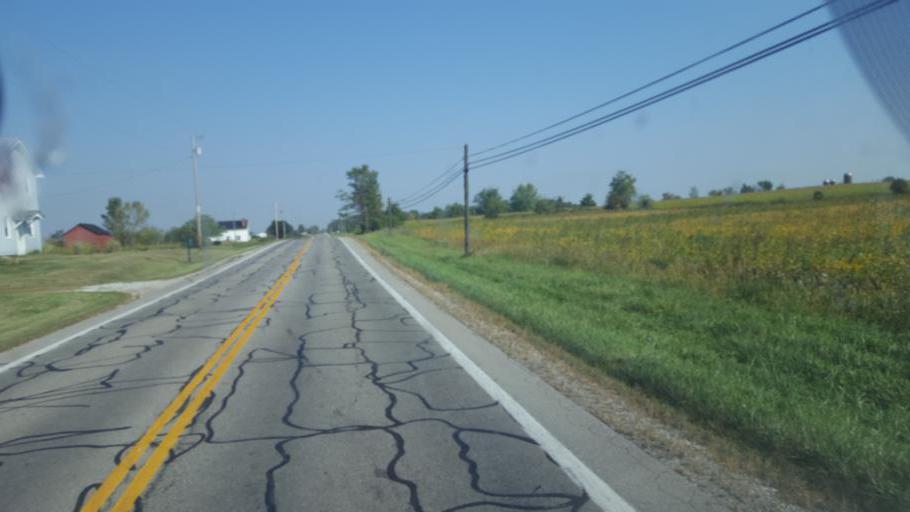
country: US
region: Ohio
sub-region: Morrow County
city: Mount Gilead
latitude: 40.6287
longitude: -82.8227
